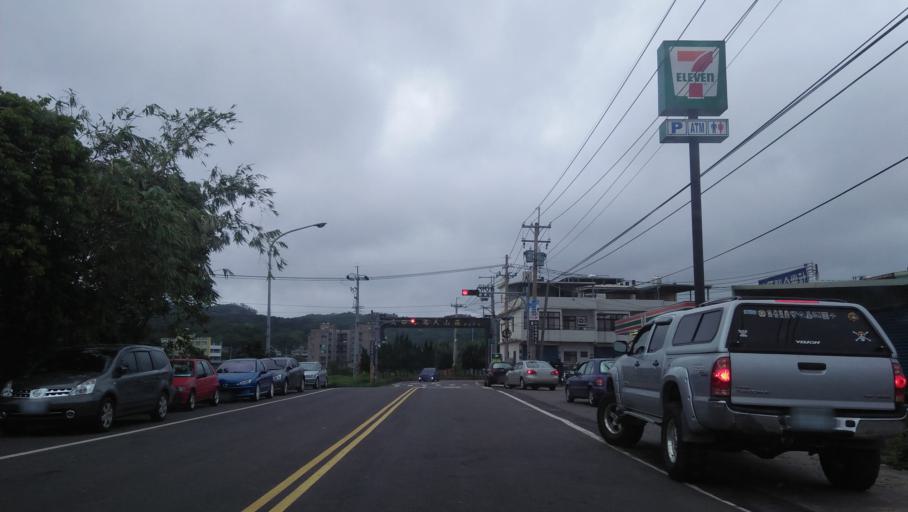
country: TW
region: Taiwan
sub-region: Hsinchu
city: Zhubei
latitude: 24.7889
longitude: 121.0672
